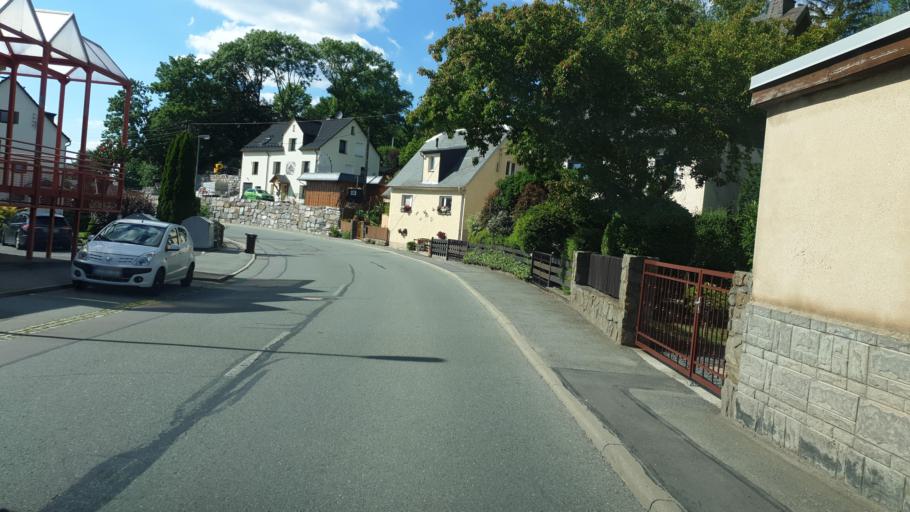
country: DE
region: Saxony
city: Burkhardtsdorf
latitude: 50.7635
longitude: 12.9094
